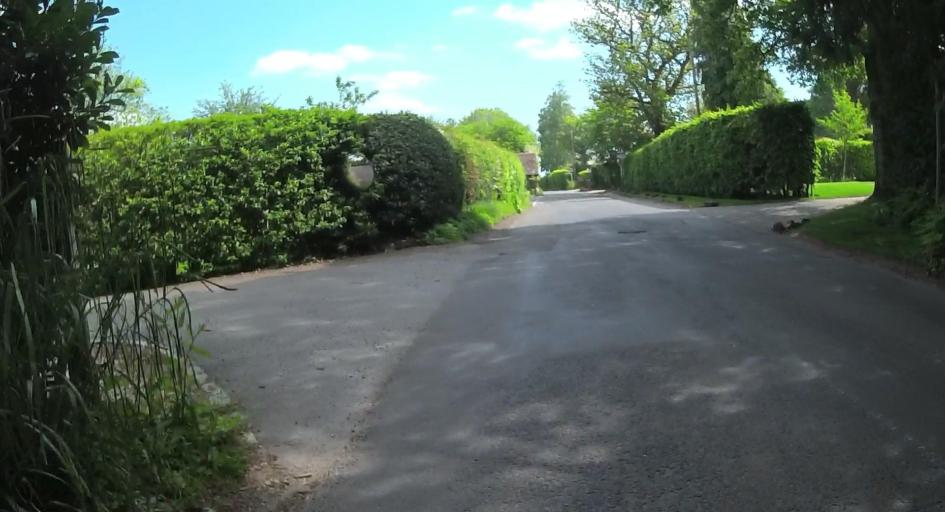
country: GB
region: England
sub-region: Surrey
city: Farnham
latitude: 51.1895
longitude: -0.8052
